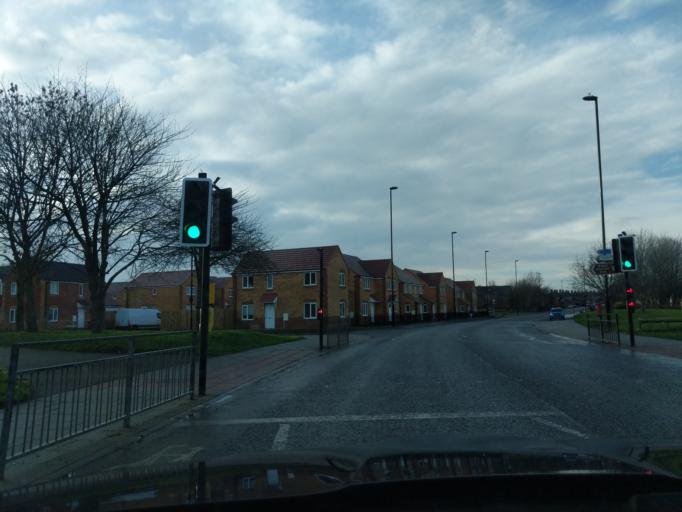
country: GB
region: England
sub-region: Gateshead
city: Felling
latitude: 54.9650
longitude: -1.5517
